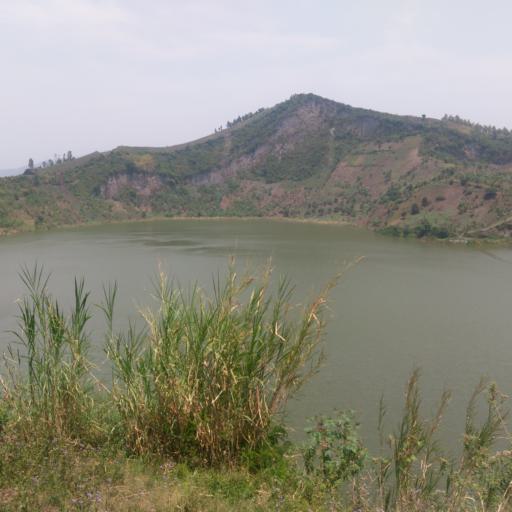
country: CD
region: Nord Kivu
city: Sake
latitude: -1.6127
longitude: 29.1385
